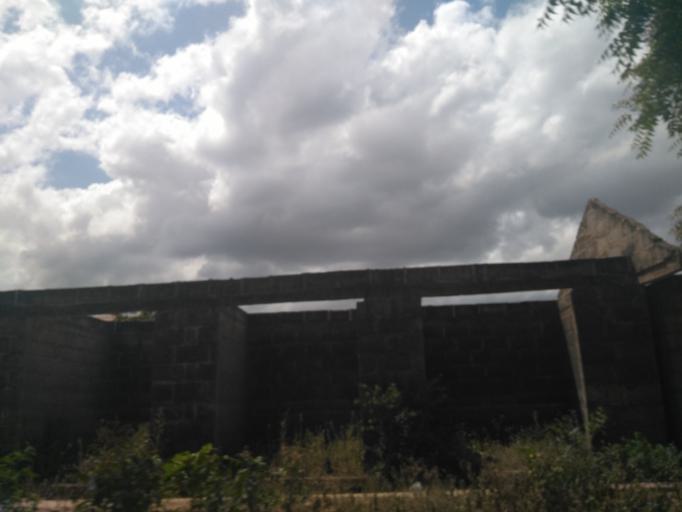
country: TZ
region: Dar es Salaam
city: Dar es Salaam
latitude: -6.9064
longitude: 39.2368
